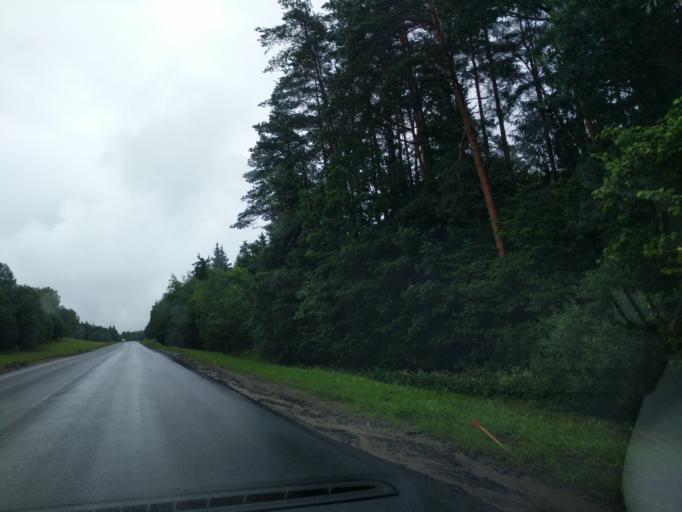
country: BY
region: Minsk
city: Syomkava
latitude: 54.2411
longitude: 27.4852
